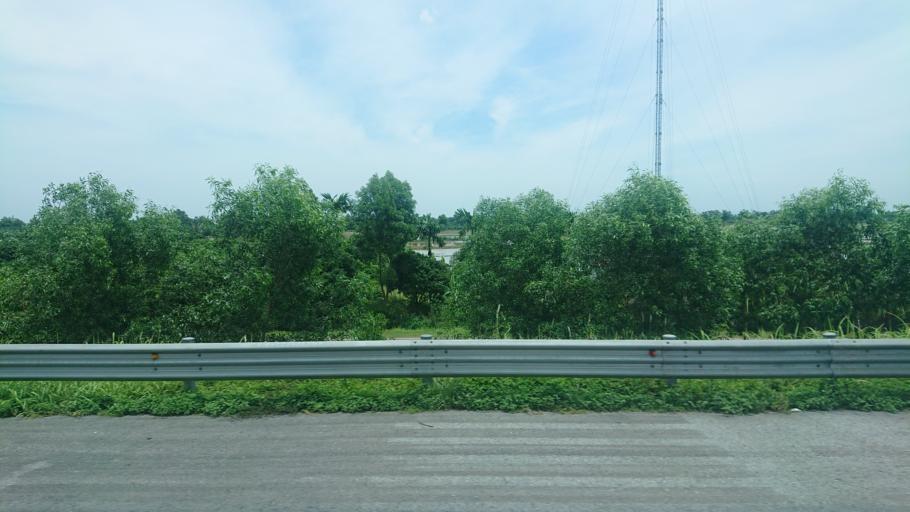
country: VN
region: Hai Duong
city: Tu Ky
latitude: 20.8368
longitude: 106.4301
